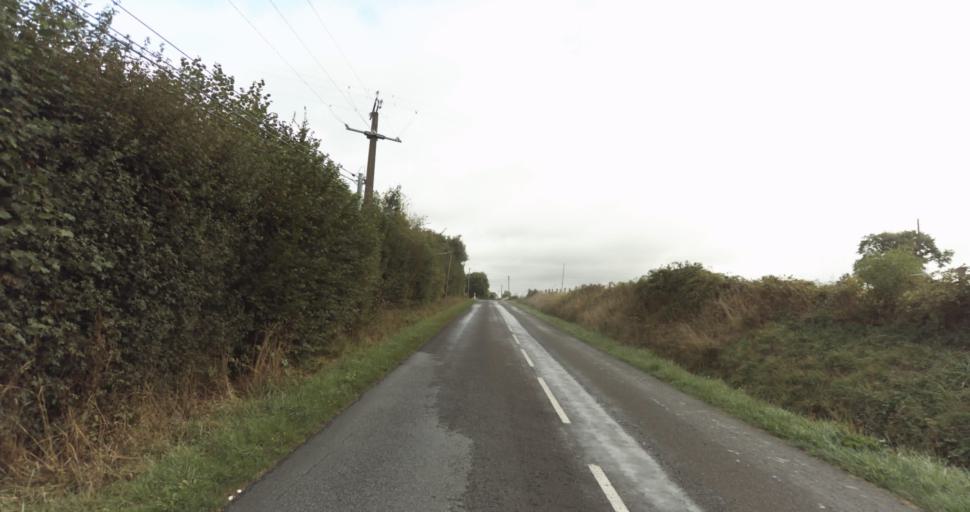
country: FR
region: Lower Normandy
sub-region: Departement de l'Orne
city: Sainte-Gauburge-Sainte-Colombe
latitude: 48.7276
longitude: 0.4327
